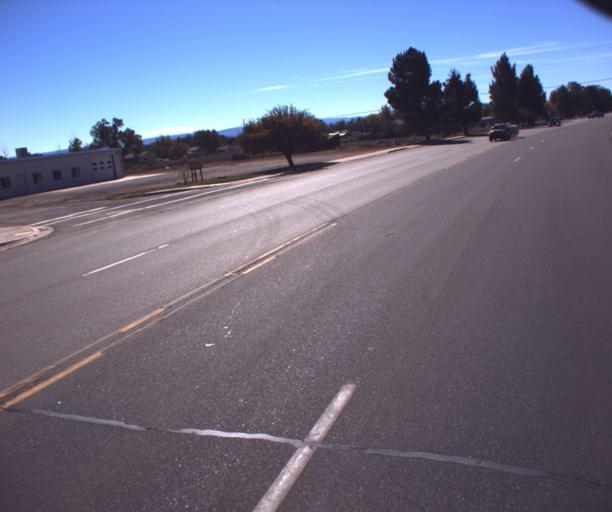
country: US
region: Arizona
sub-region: Coconino County
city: Fredonia
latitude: 36.9543
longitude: -112.5266
